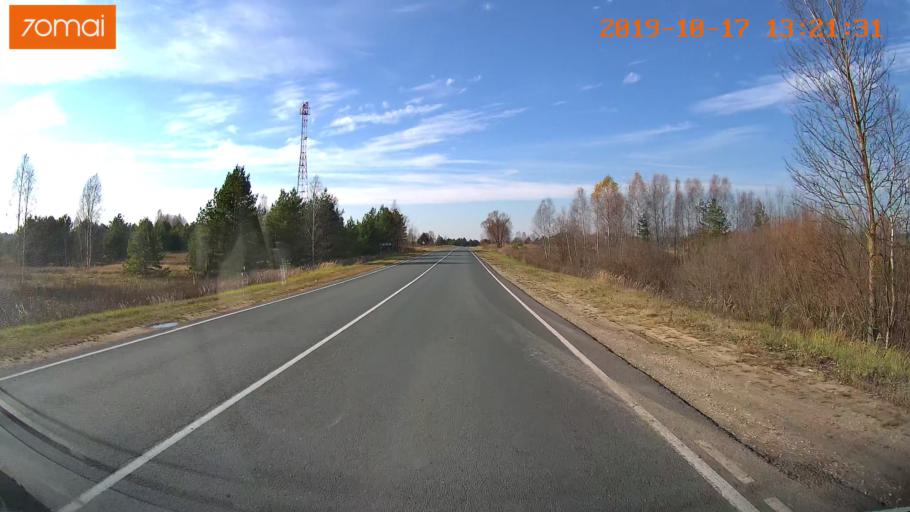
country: RU
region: Rjazan
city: Gus'-Zheleznyy
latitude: 55.0813
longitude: 41.0250
